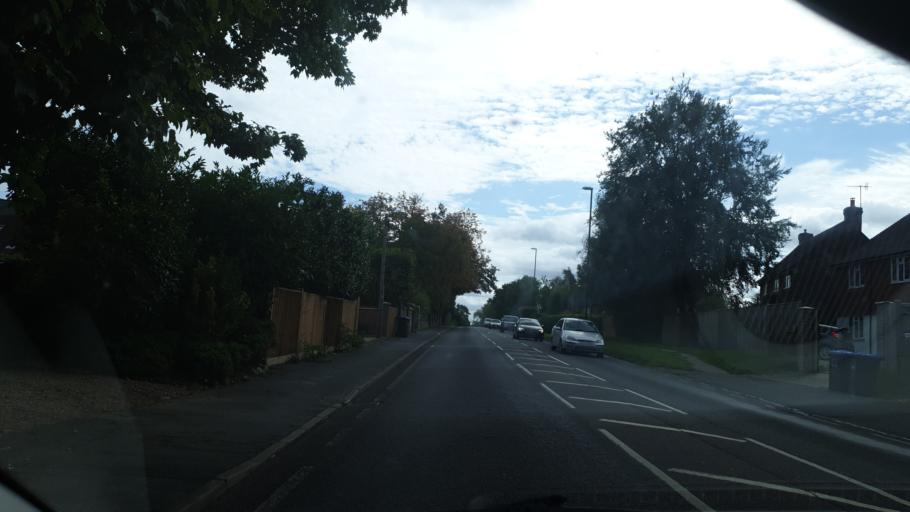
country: GB
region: England
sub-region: West Sussex
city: East Grinstead
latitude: 51.1162
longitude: 0.0141
